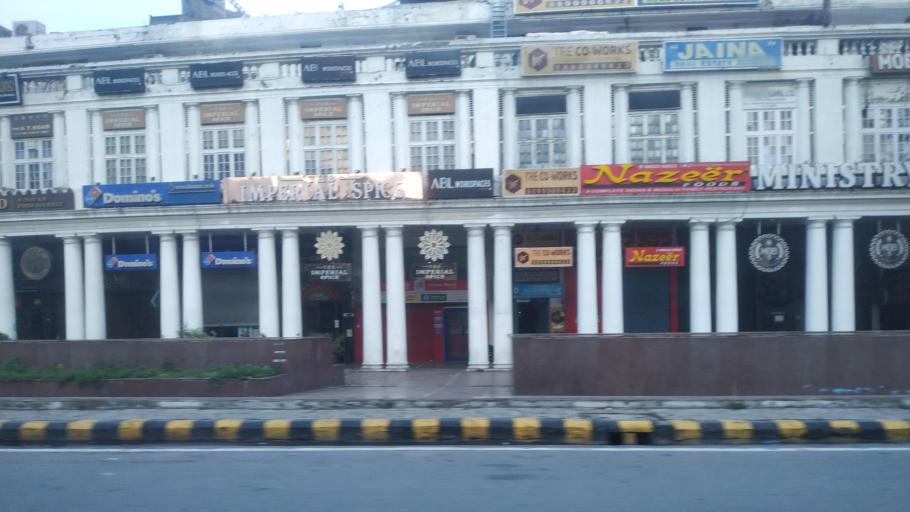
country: IN
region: NCT
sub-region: New Delhi
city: New Delhi
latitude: 28.6331
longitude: 77.2229
